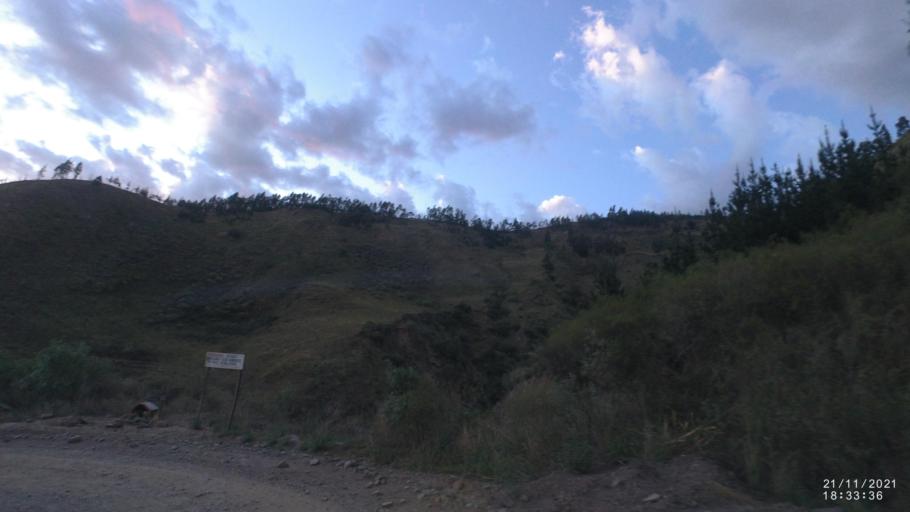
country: BO
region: Cochabamba
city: Cochabamba
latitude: -17.3087
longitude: -66.2204
